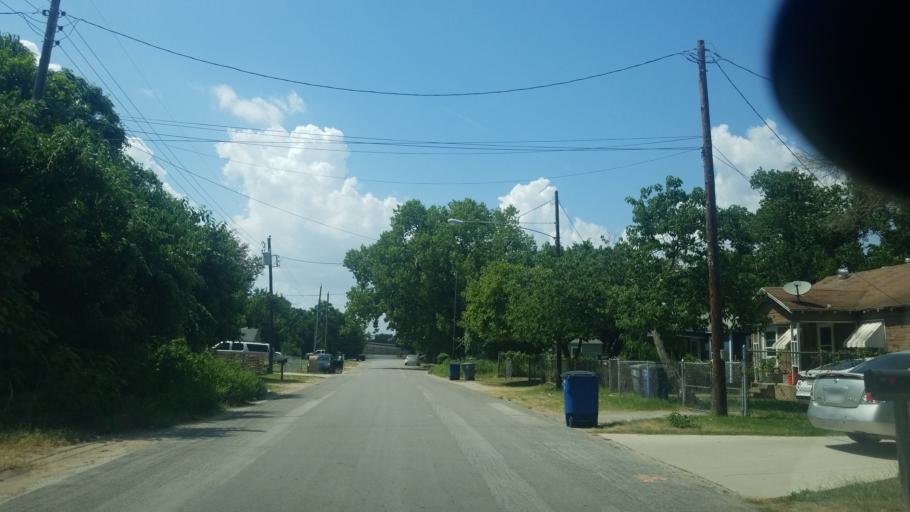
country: US
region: Texas
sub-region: Dallas County
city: Hutchins
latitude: 32.7160
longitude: -96.7492
